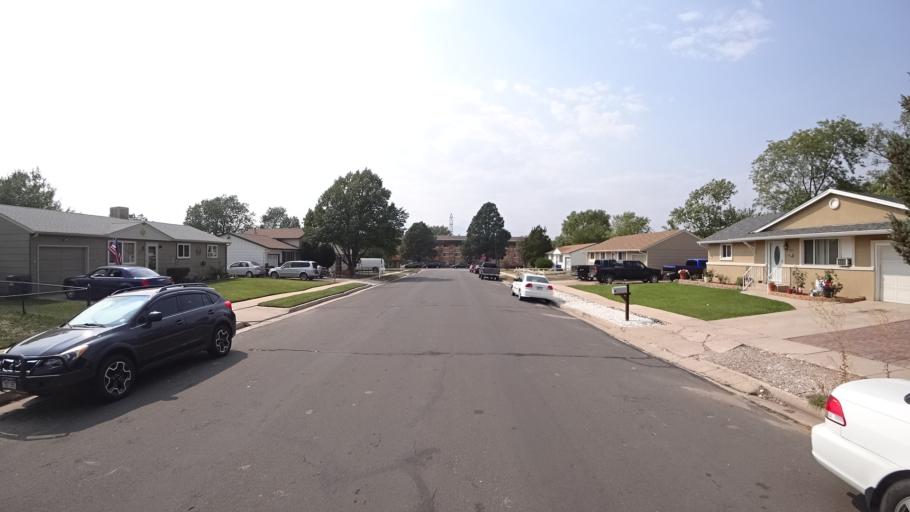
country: US
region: Colorado
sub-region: El Paso County
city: Stratmoor
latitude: 38.8303
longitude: -104.7550
